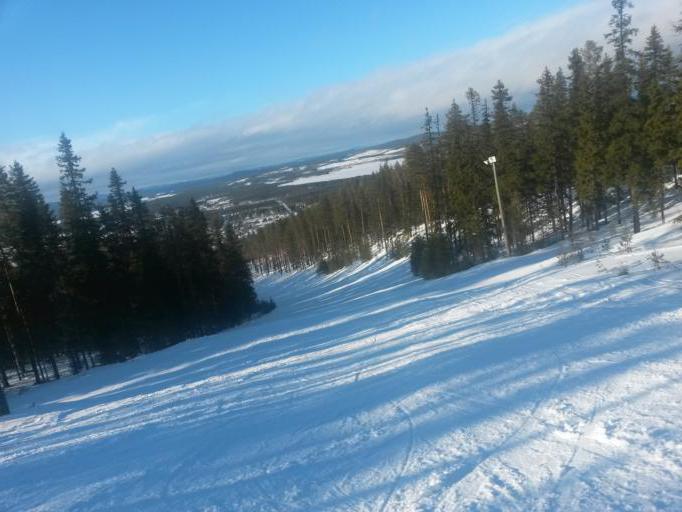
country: SE
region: Vaesterbotten
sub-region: Mala Kommun
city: Mala
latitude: 65.1791
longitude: 18.7648
